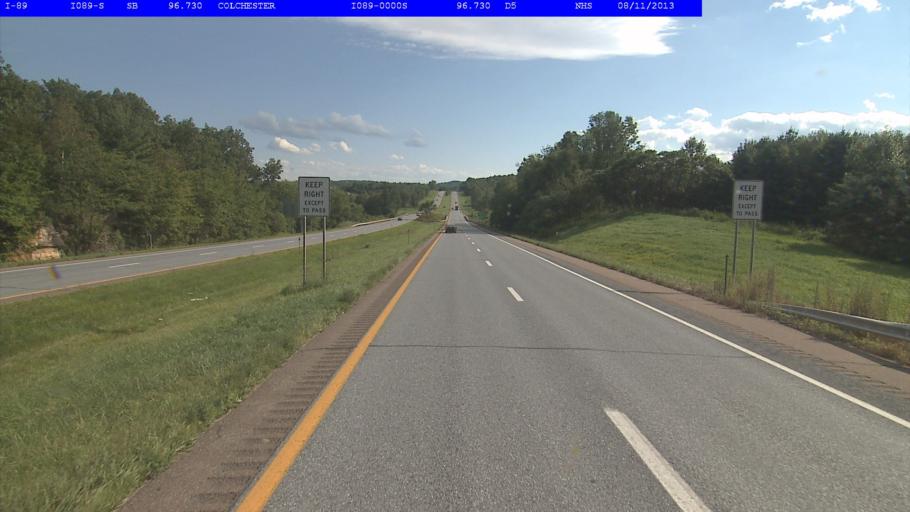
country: US
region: Vermont
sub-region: Chittenden County
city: Colchester
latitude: 44.5743
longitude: -73.1775
